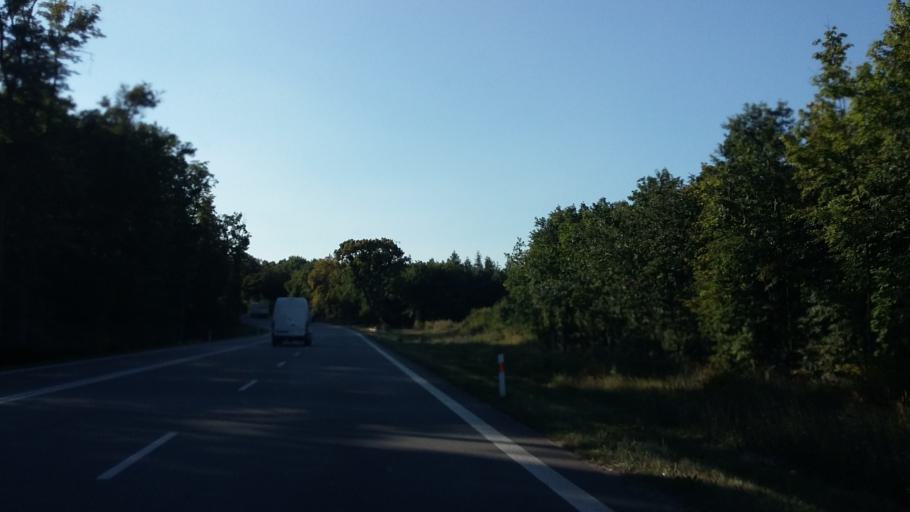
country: CZ
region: South Moravian
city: Troubsko
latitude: 49.1877
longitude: 16.4700
